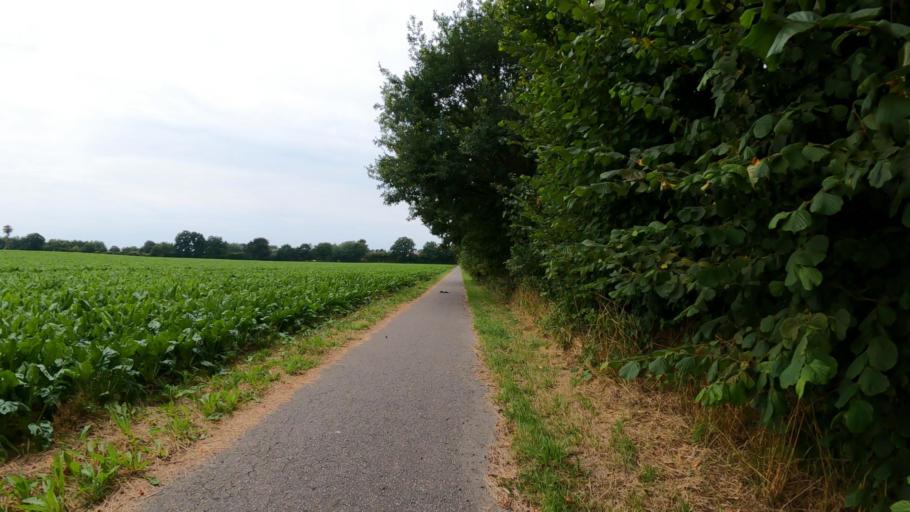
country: DE
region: Schleswig-Holstein
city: Leezen
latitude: 53.8686
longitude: 10.2334
